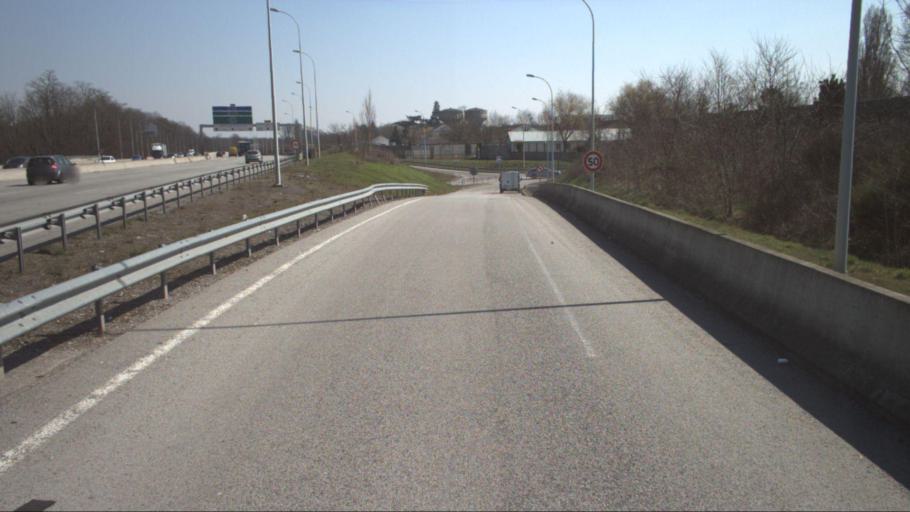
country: FR
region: Ile-de-France
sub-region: Departement des Yvelines
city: Buc
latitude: 48.7899
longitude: 2.1162
